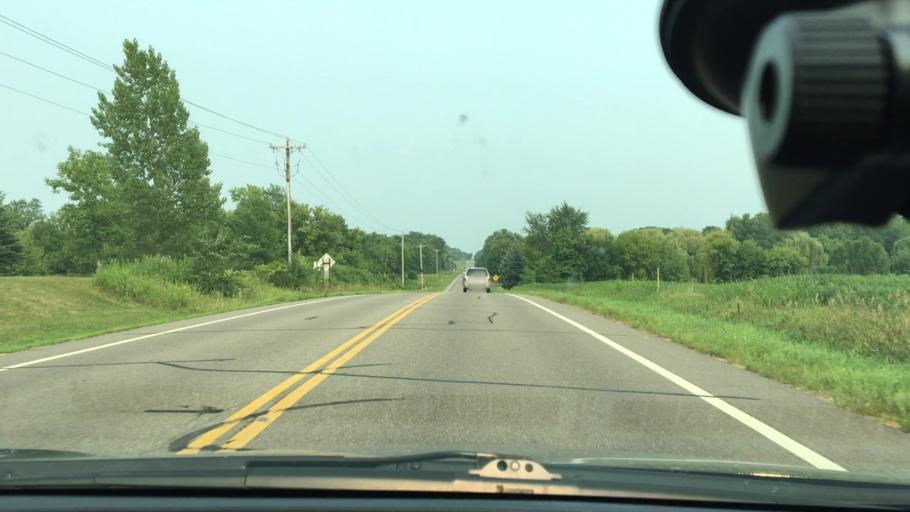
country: US
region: Minnesota
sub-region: Hennepin County
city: Champlin
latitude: 45.1881
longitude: -93.4591
